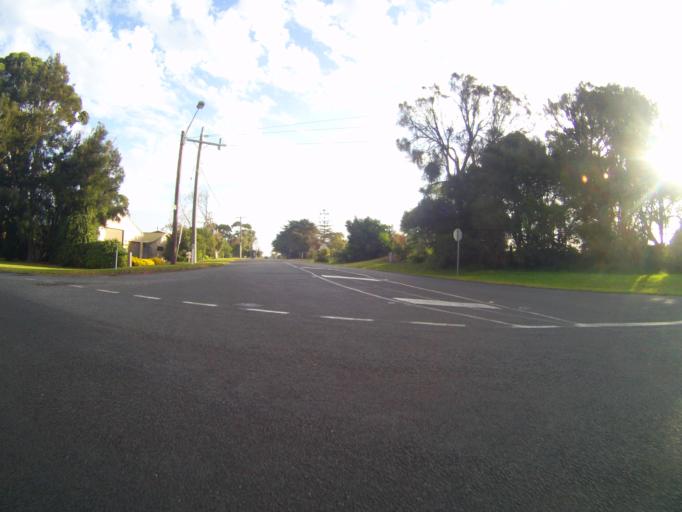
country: AU
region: Victoria
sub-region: Queenscliffe
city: Queenscliff
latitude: -38.2665
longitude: 144.6186
